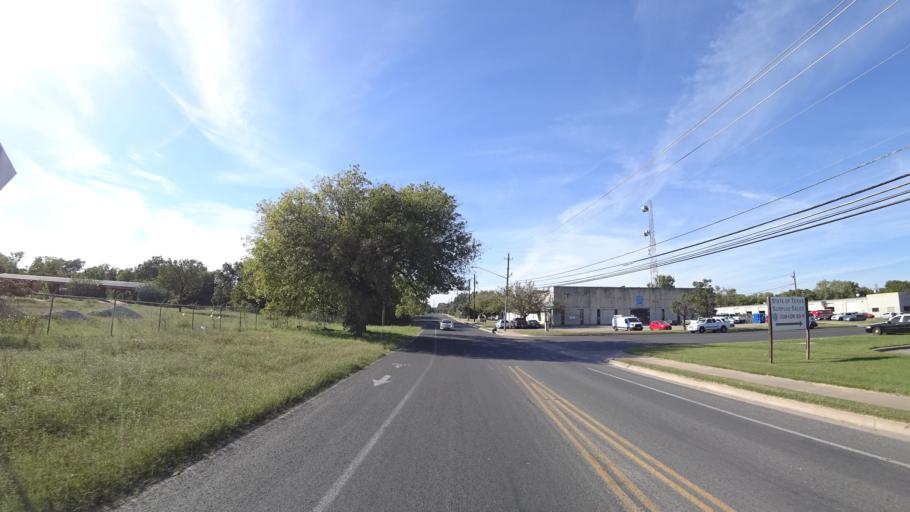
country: US
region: Texas
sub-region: Travis County
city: Austin
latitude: 30.2541
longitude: -97.6812
